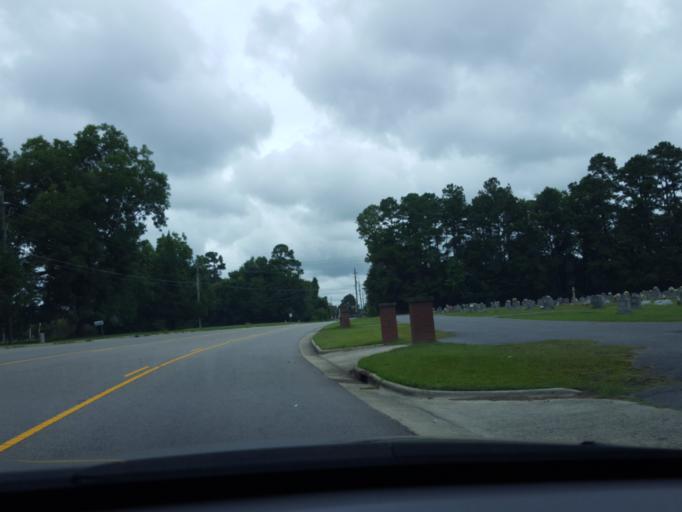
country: US
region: North Carolina
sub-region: Martin County
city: Williamston
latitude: 35.8032
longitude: -76.9011
